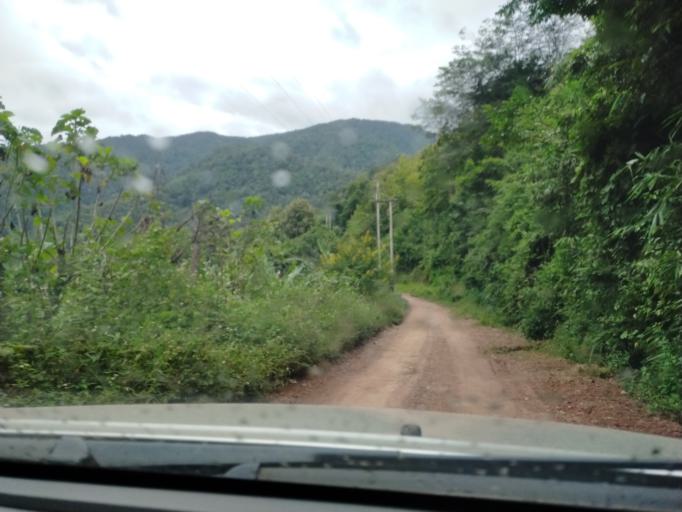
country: TH
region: Nan
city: Chaloem Phra Kiat
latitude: 19.8143
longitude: 101.3593
